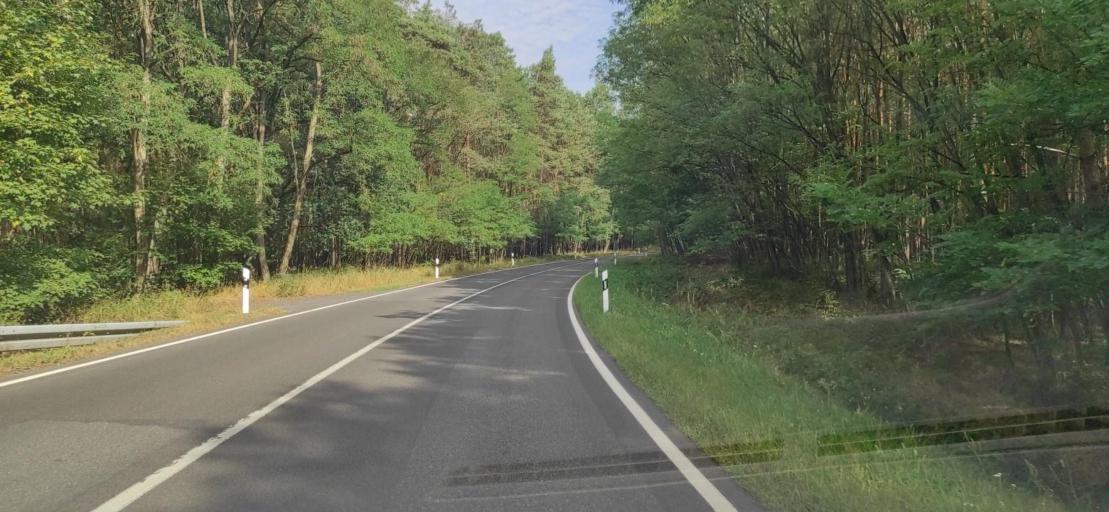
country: DE
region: Brandenburg
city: Forst
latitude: 51.6821
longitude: 14.7224
